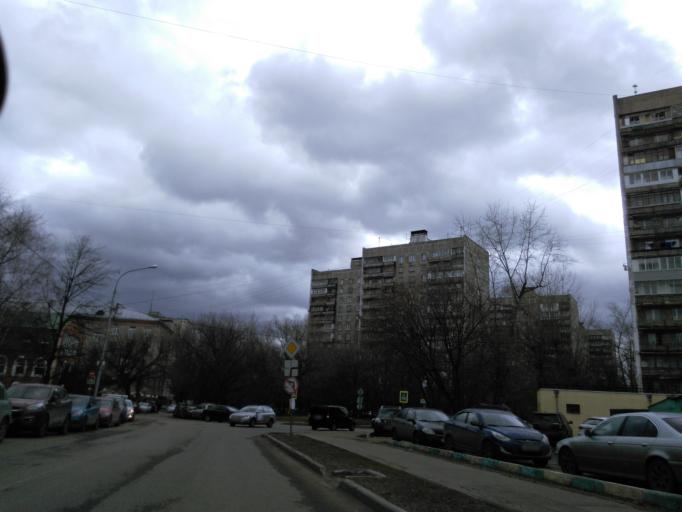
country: RU
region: Moskovskaya
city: Koptevo
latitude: 55.8193
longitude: 37.5181
